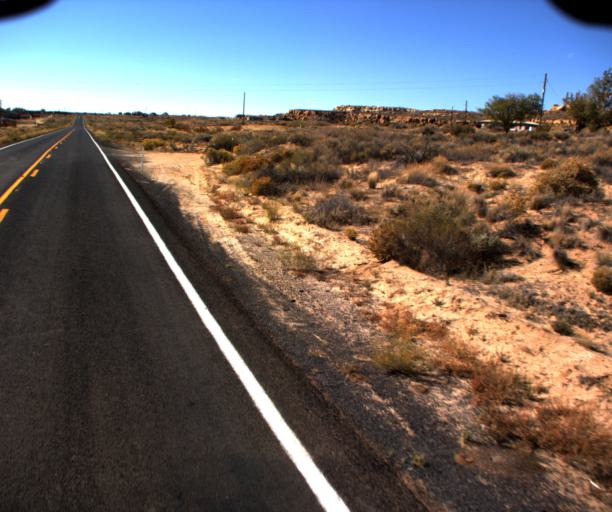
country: US
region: Arizona
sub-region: Navajo County
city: First Mesa
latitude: 35.8845
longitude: -110.6360
